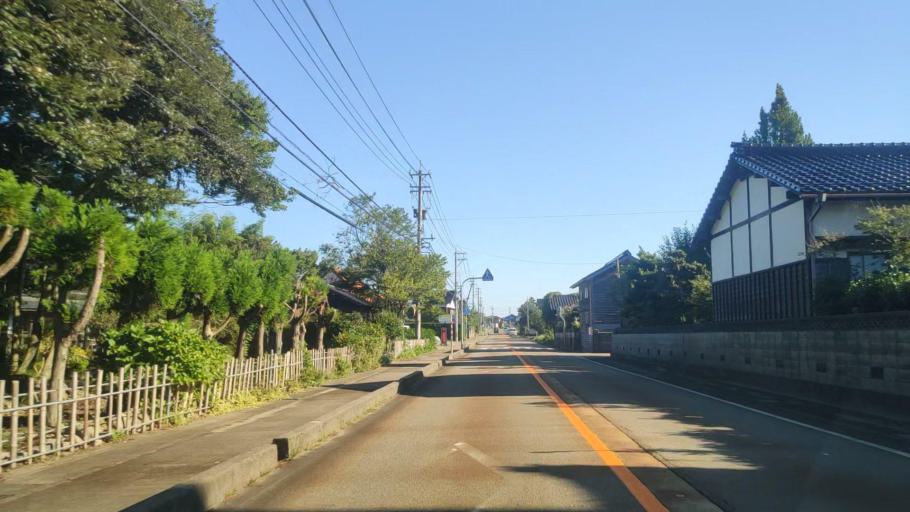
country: JP
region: Ishikawa
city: Hakui
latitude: 36.8399
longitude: 136.7638
